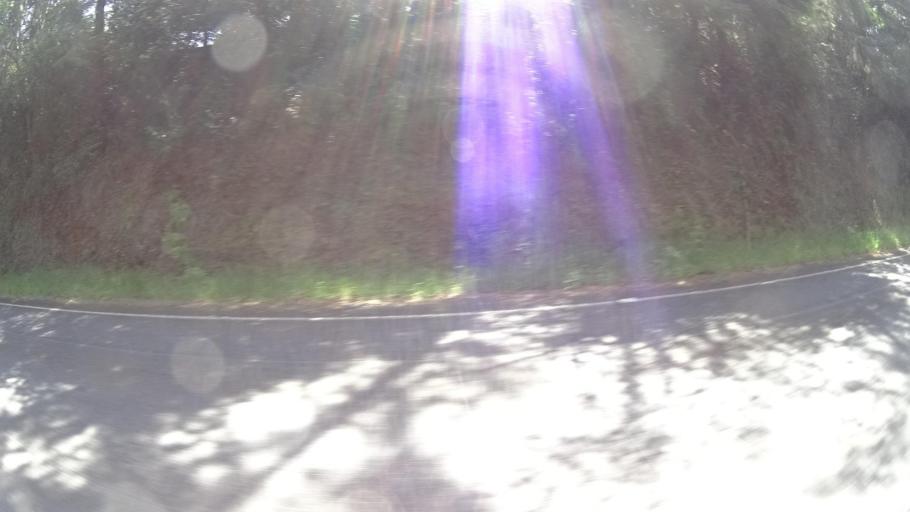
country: US
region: California
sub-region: Humboldt County
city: Humboldt Hill
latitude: 40.6514
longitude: -124.2224
